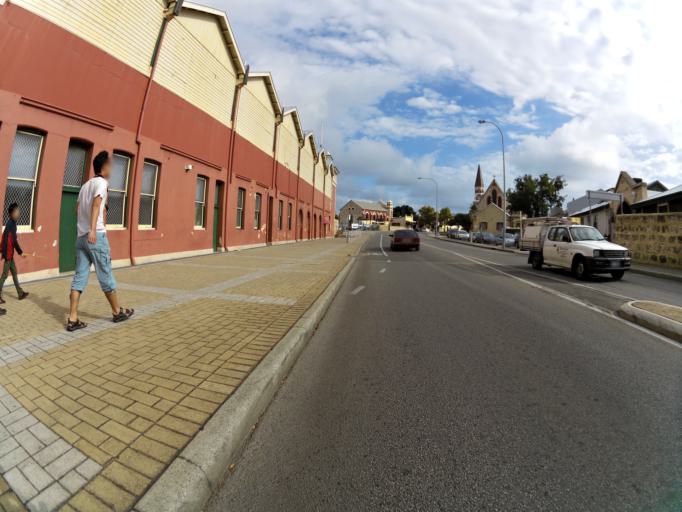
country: AU
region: Western Australia
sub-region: Fremantle
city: South Fremantle
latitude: -32.0557
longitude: 115.7501
